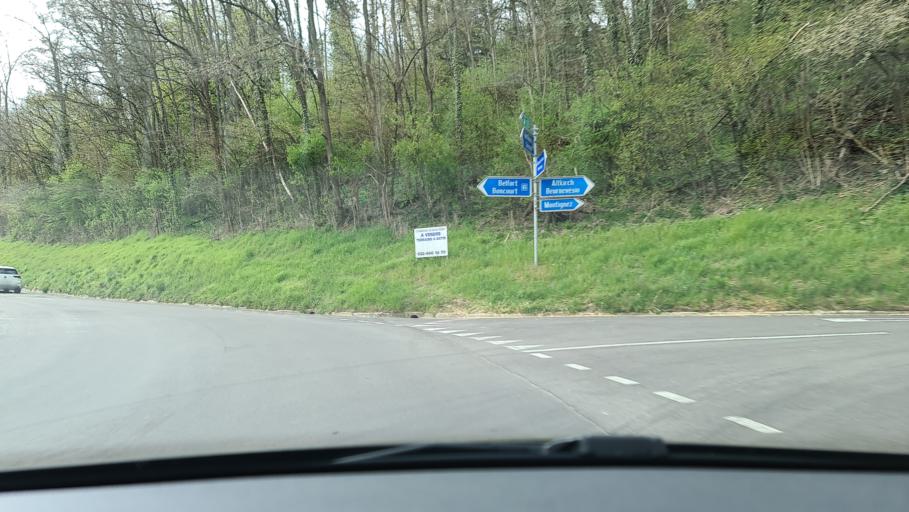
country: CH
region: Jura
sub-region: Porrentruy District
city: Boncourt
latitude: 47.4718
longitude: 7.0470
